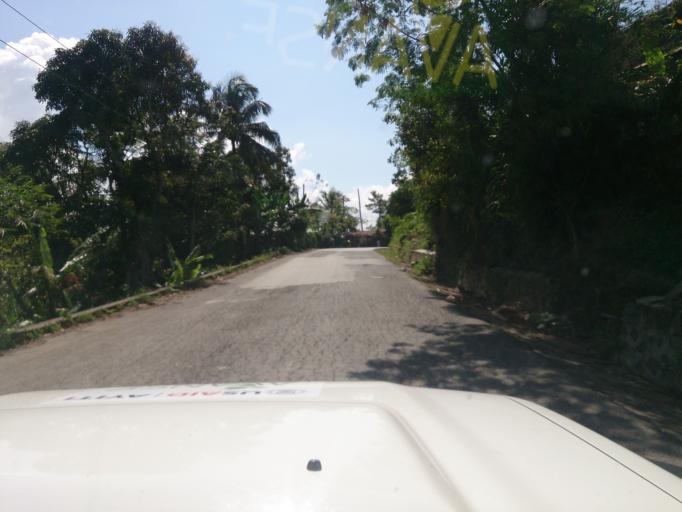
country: HT
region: Nord
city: Plaisance
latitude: 19.6079
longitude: -72.4506
